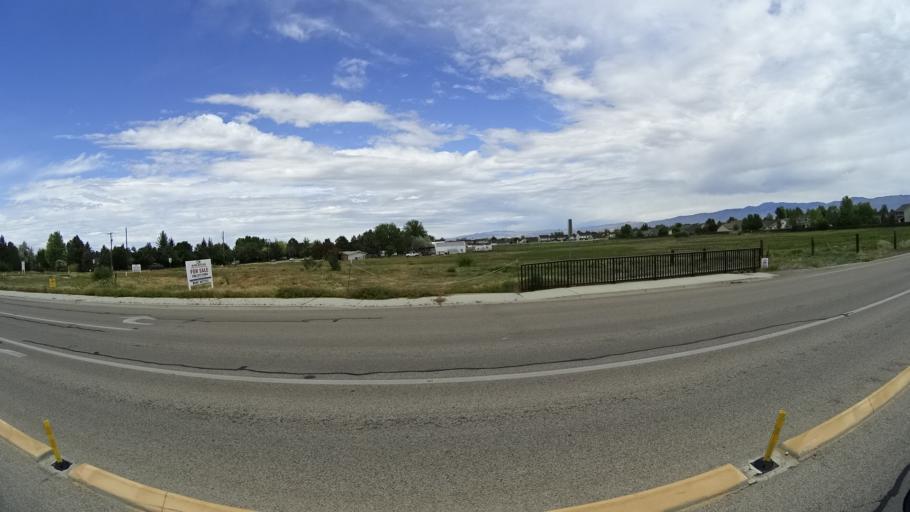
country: US
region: Idaho
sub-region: Ada County
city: Meridian
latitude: 43.5756
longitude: -116.3535
